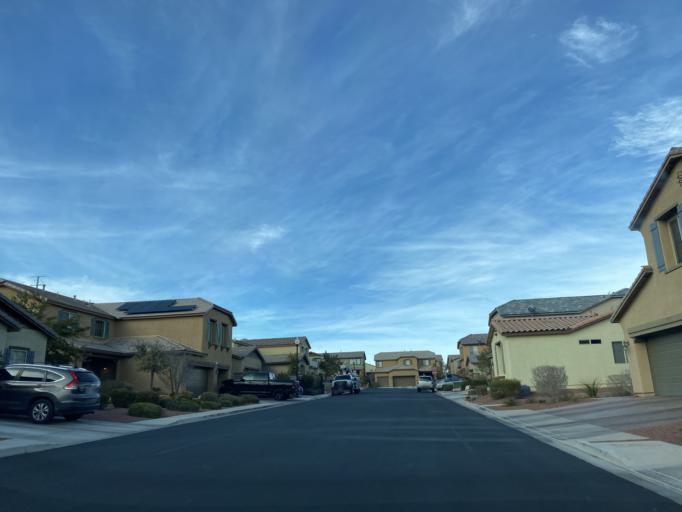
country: US
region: Nevada
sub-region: Clark County
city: Summerlin South
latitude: 36.2778
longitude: -115.3321
